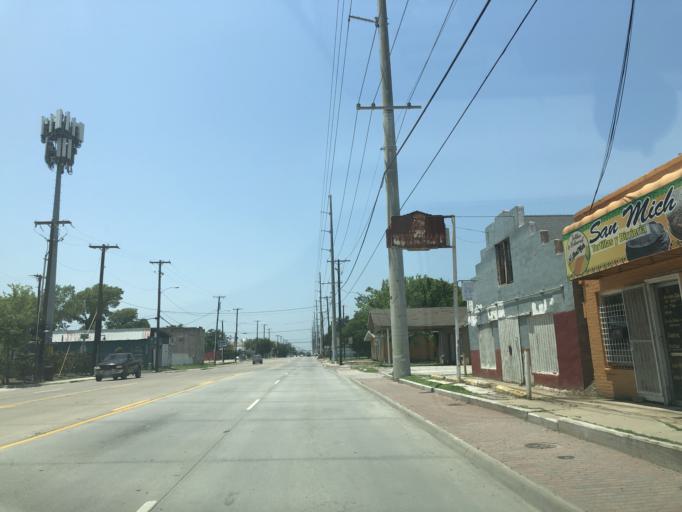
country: US
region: Texas
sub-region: Dallas County
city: Dallas
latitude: 32.7786
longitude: -96.8414
